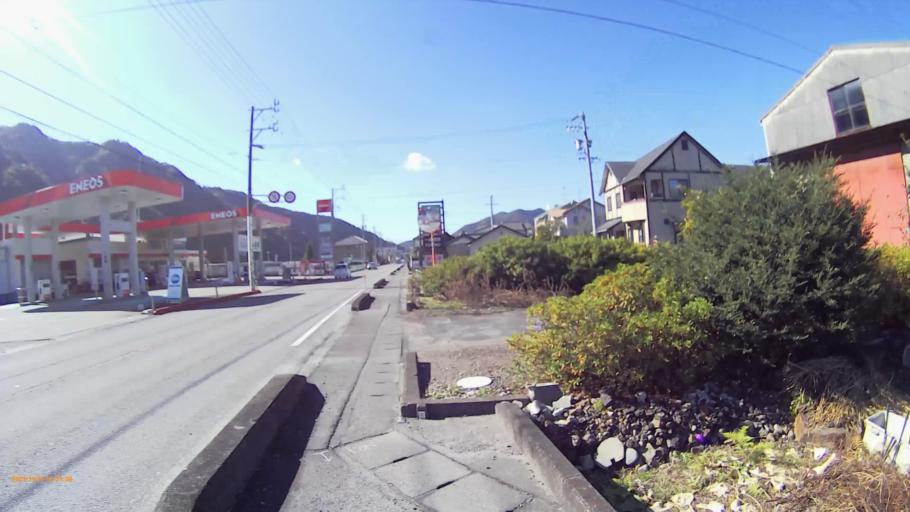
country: JP
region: Gifu
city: Inuyama
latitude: 35.4267
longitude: 136.9876
